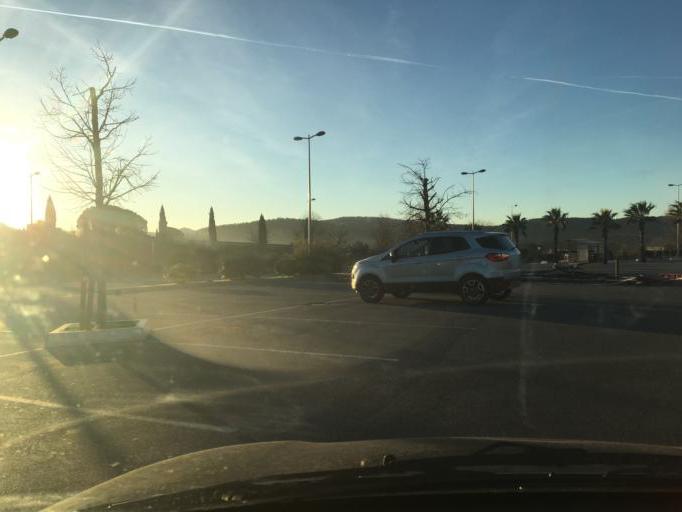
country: FR
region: Provence-Alpes-Cote d'Azur
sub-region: Departement du Var
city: Les Arcs
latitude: 43.4511
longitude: 6.4911
